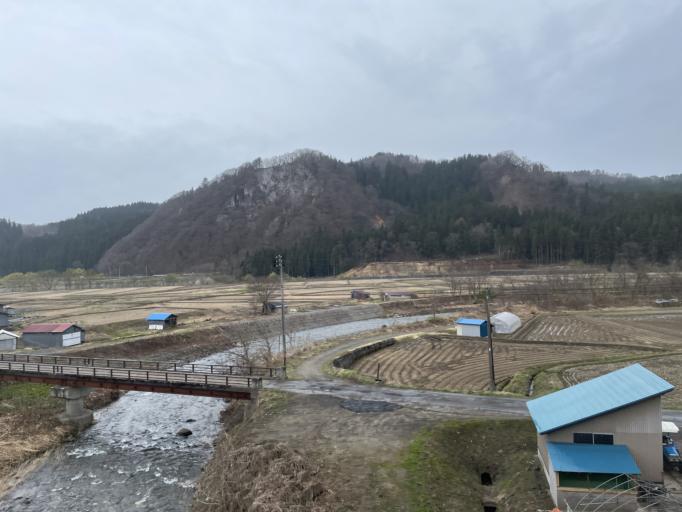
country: JP
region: Akita
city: Takanosu
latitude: 40.0415
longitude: 140.3998
